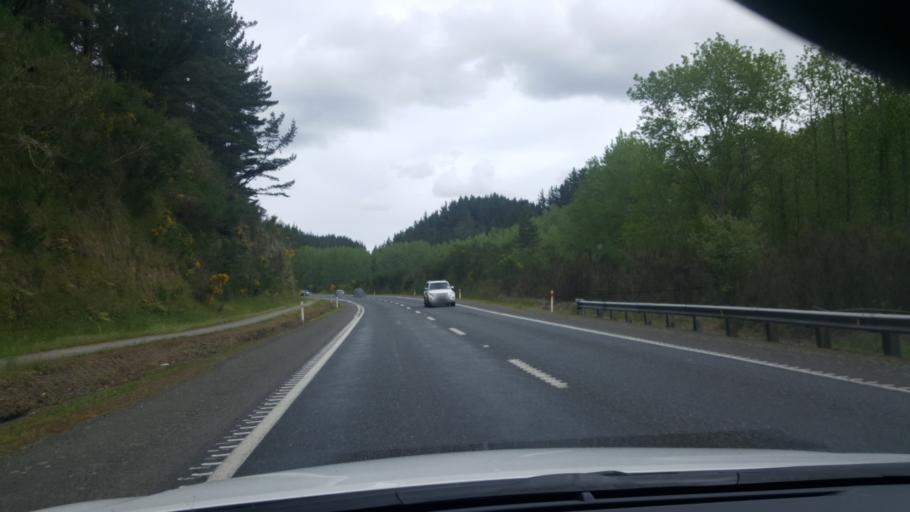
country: NZ
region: Bay of Plenty
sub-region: Rotorua District
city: Rotorua
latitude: -38.2110
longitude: 176.2619
